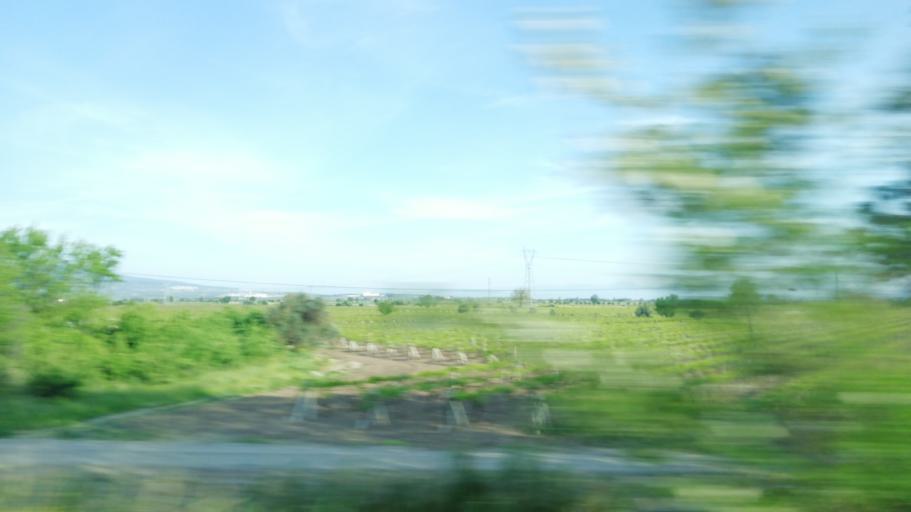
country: TR
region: Manisa
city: Saruhanli
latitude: 38.7194
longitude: 27.5592
